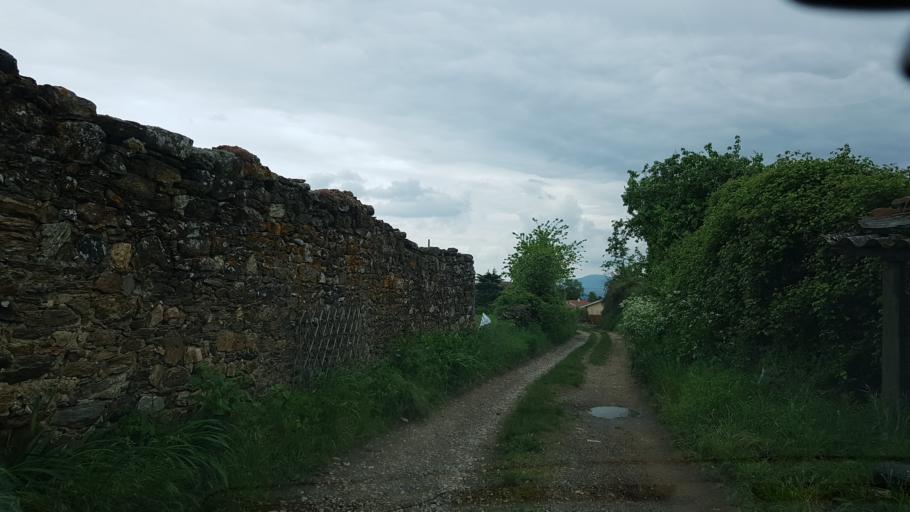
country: FR
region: Rhone-Alpes
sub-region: Departement du Rhone
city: Mornant
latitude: 45.6278
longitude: 4.6634
